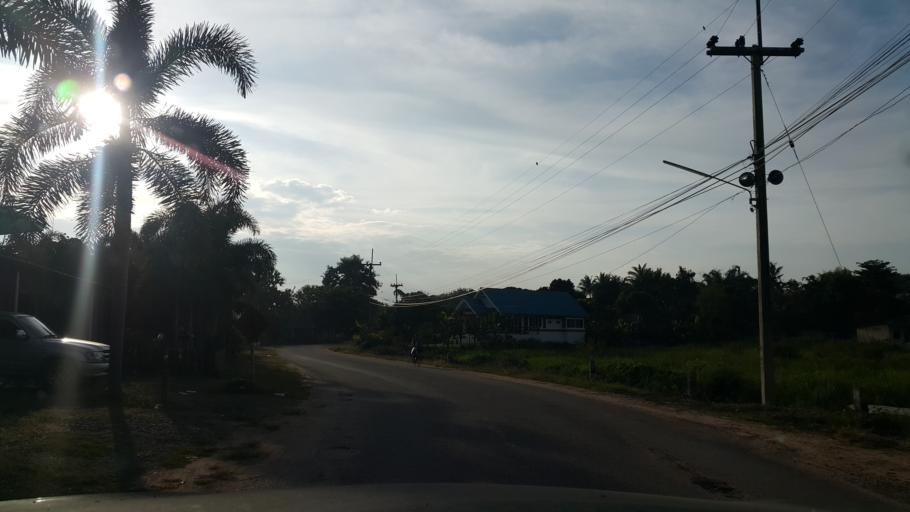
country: TH
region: Chiang Mai
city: San Sai
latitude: 18.9267
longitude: 99.0399
